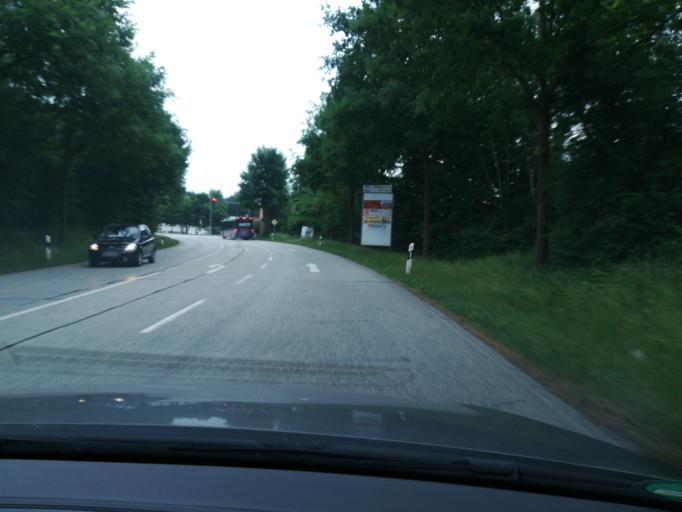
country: DE
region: Schleswig-Holstein
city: Schwarzenbek
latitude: 53.5069
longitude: 10.4747
